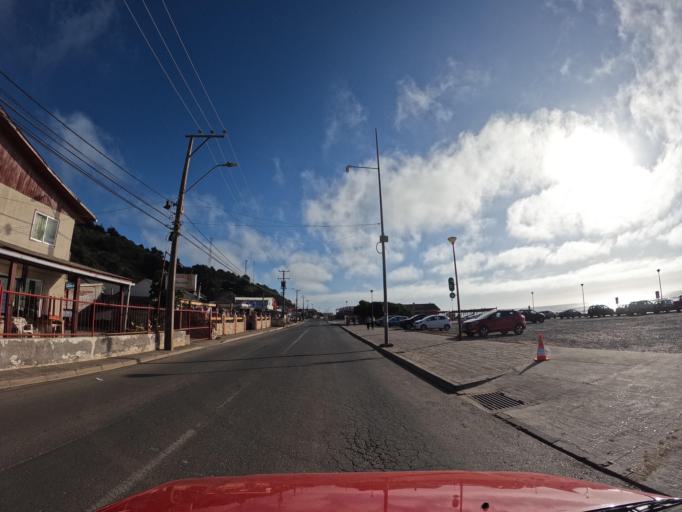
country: CL
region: Maule
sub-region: Provincia de Talca
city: Constitucion
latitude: -34.9368
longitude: -72.1816
